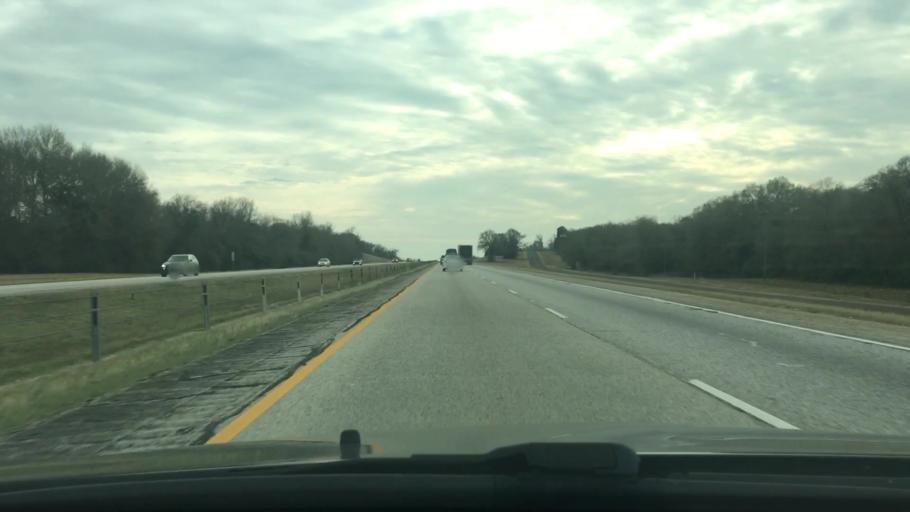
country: US
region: Texas
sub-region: Leon County
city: Centerville
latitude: 31.2296
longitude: -95.9947
